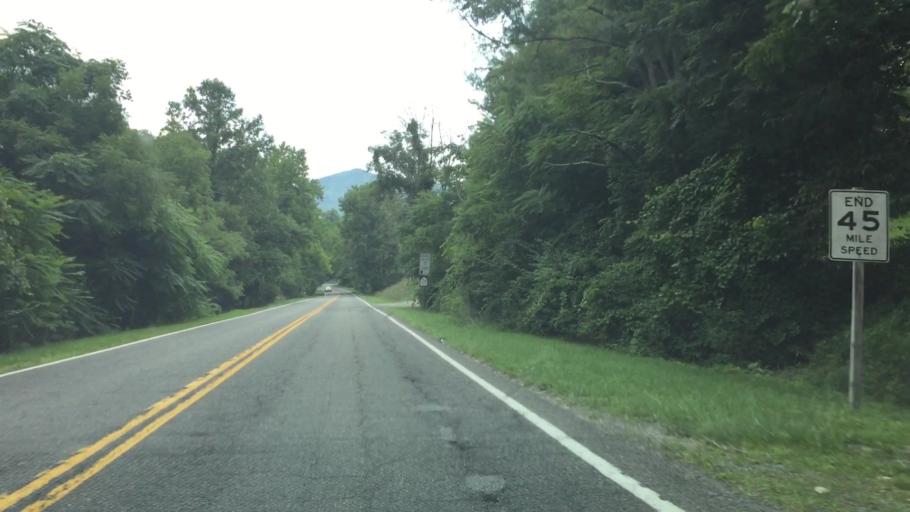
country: US
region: Virginia
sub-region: Pulaski County
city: Dublin
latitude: 37.0673
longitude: -80.7021
